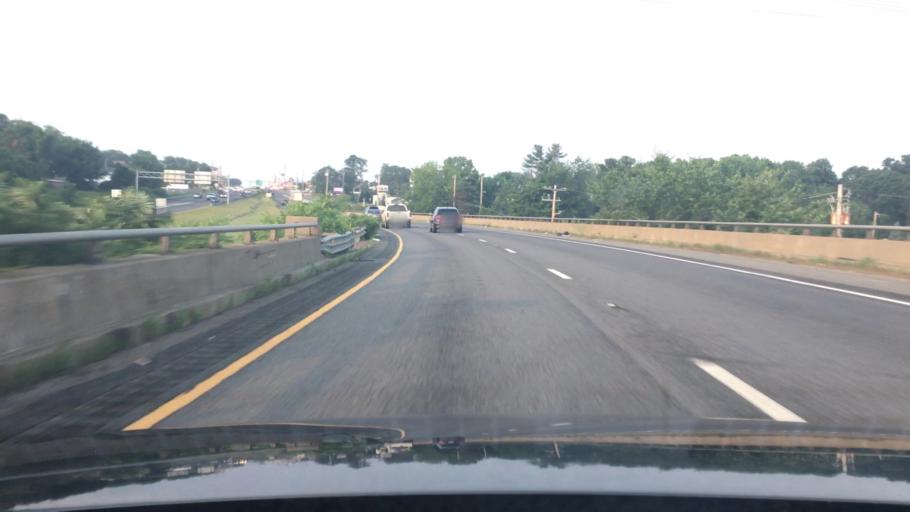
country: US
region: Massachusetts
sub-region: Essex County
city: South Peabody
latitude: 42.5428
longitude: -70.9855
